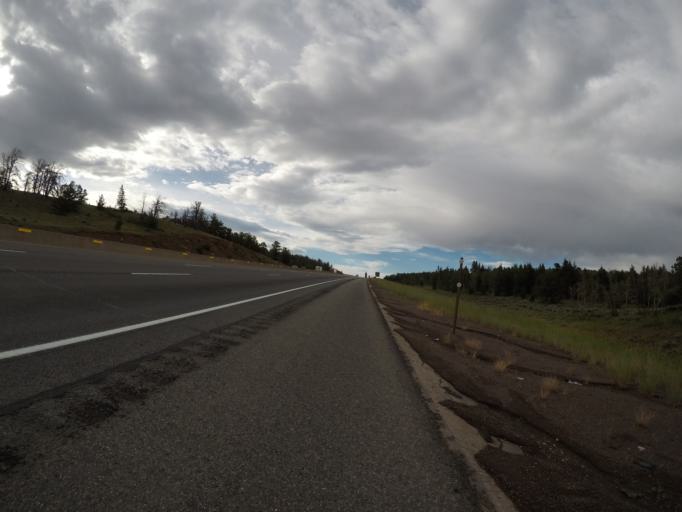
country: US
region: Wyoming
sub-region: Albany County
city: Laramie
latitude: 41.2528
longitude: -105.4461
